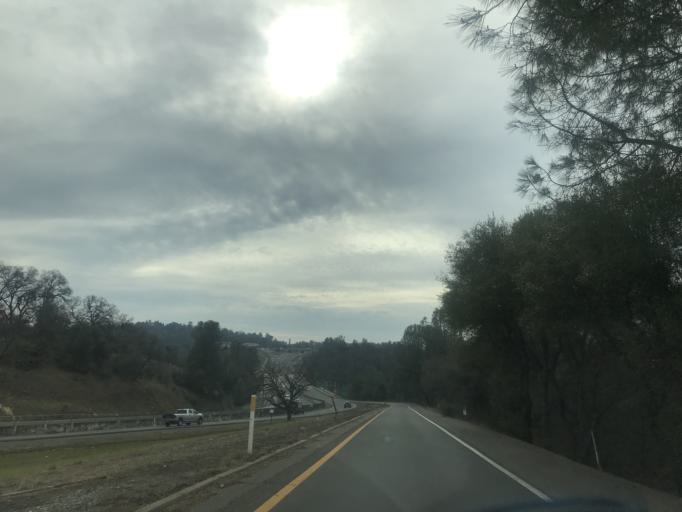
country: US
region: California
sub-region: El Dorado County
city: Diamond Springs
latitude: 38.7216
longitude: -120.8343
